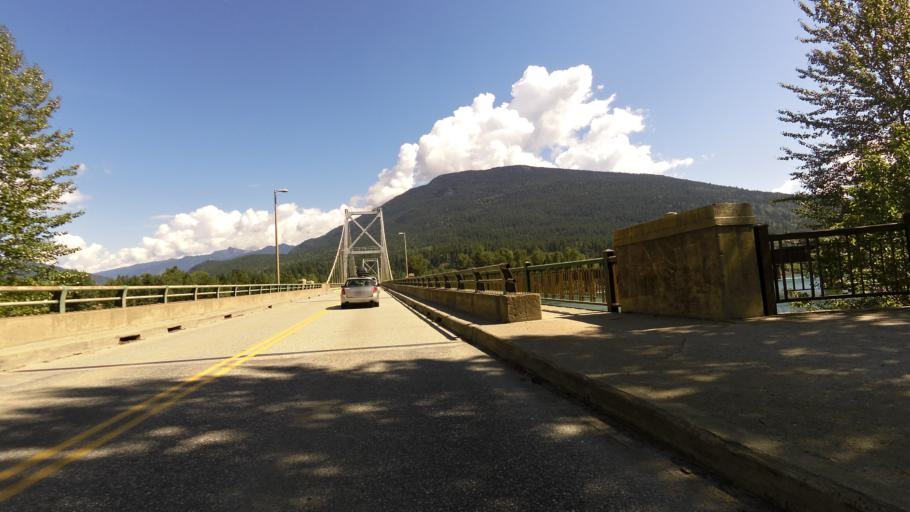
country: CA
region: British Columbia
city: Revelstoke
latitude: 51.0051
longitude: -118.2219
